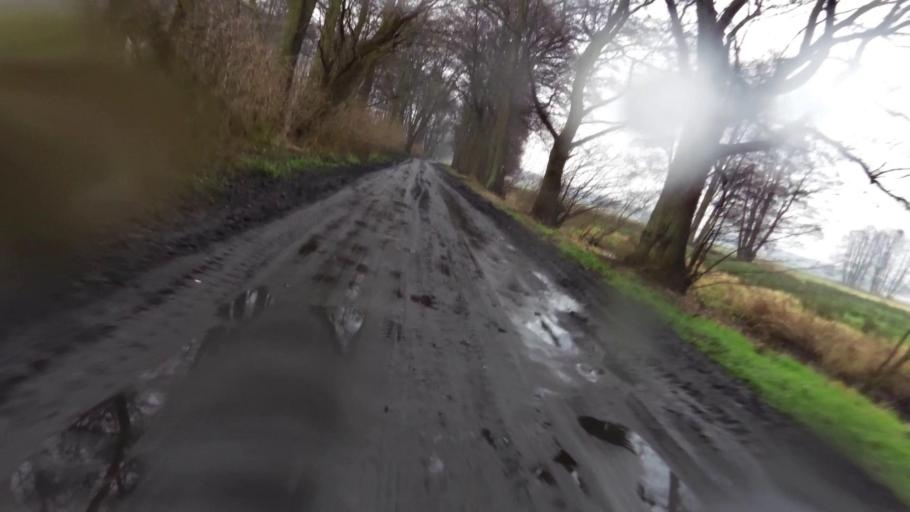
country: PL
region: West Pomeranian Voivodeship
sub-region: Powiat goleniowski
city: Goleniow
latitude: 53.4392
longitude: 14.7206
